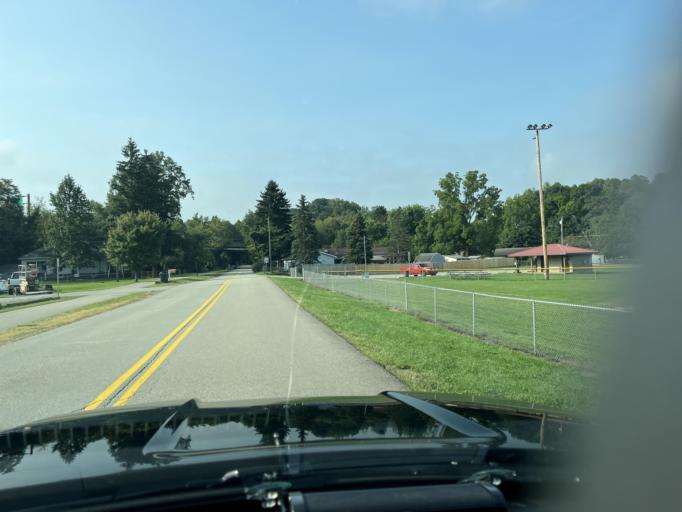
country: US
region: Pennsylvania
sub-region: Fayette County
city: Hopwood
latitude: 39.8725
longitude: -79.7144
